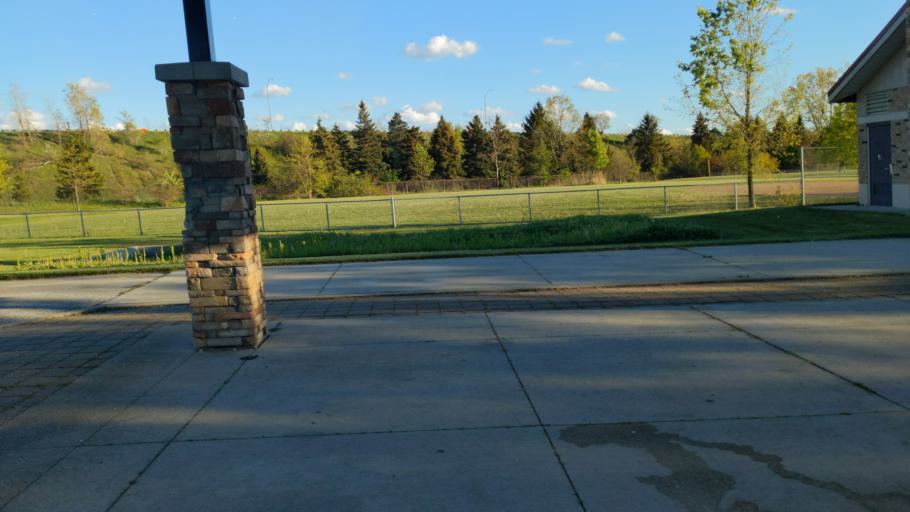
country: US
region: Ohio
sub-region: Cuyahoga County
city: Brooklyn
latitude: 41.4746
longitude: -81.7278
